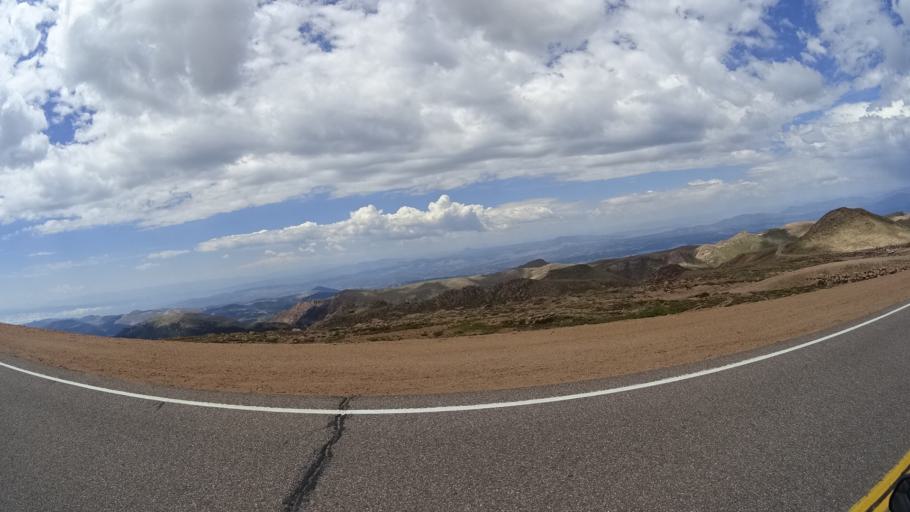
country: US
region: Colorado
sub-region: El Paso County
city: Cascade-Chipita Park
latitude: 38.8440
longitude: -105.0503
